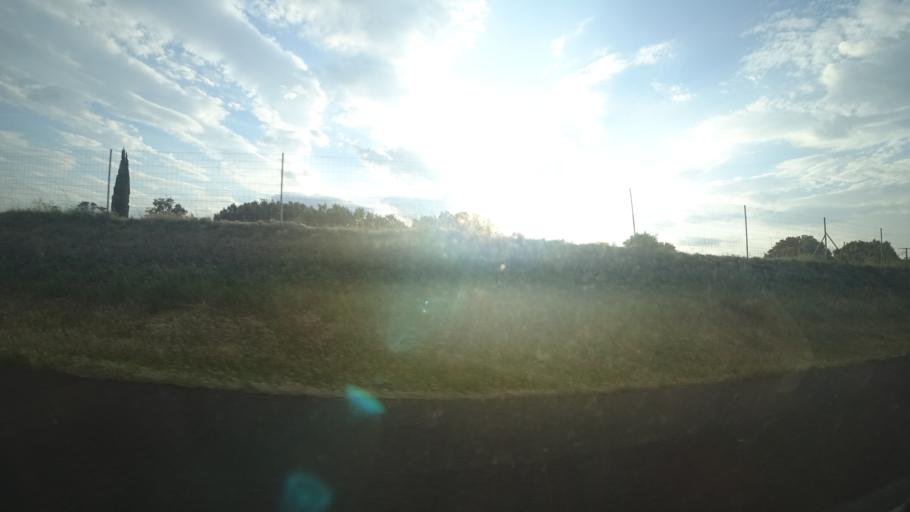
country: FR
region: Languedoc-Roussillon
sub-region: Departement de l'Herault
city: Aspiran
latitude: 43.5816
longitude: 3.4658
